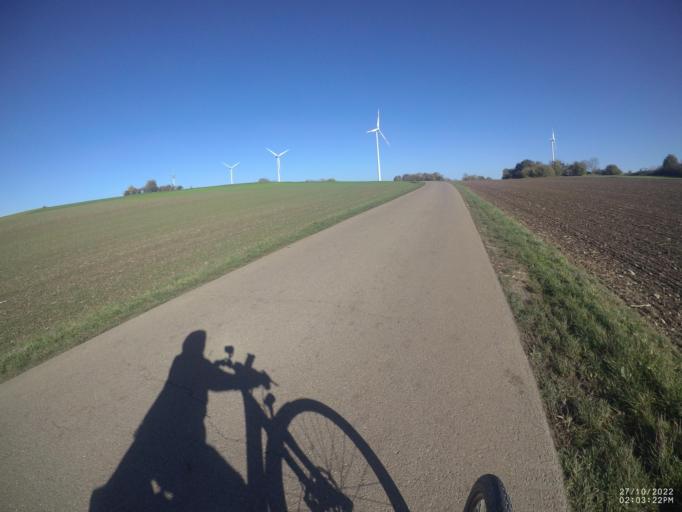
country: DE
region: Baden-Wuerttemberg
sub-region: Regierungsbezirk Stuttgart
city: Deggingen
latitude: 48.5742
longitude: 9.7432
